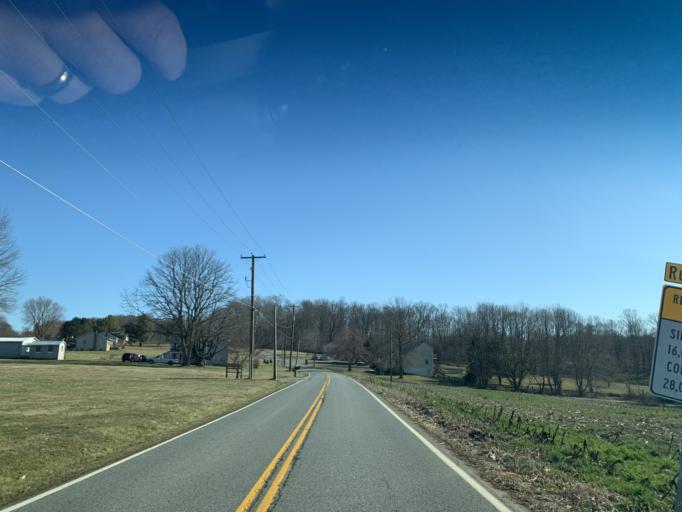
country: US
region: Maryland
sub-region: Cecil County
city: Rising Sun
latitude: 39.6519
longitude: -76.1028
